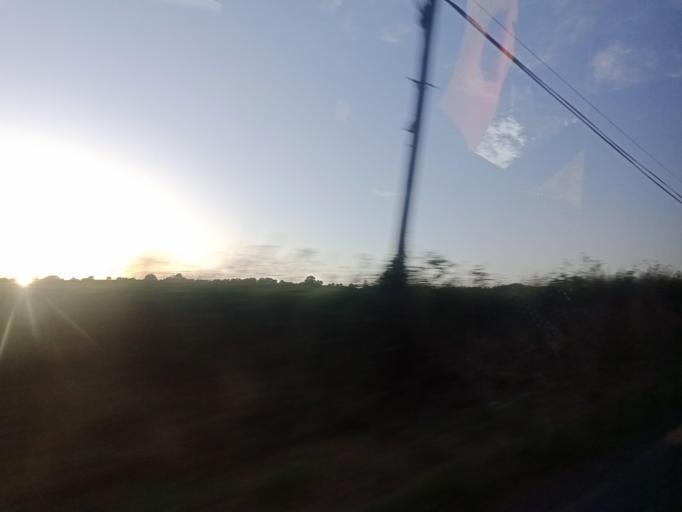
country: IE
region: Leinster
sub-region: Kilkenny
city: Castlecomer
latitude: 52.7698
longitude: -7.2200
